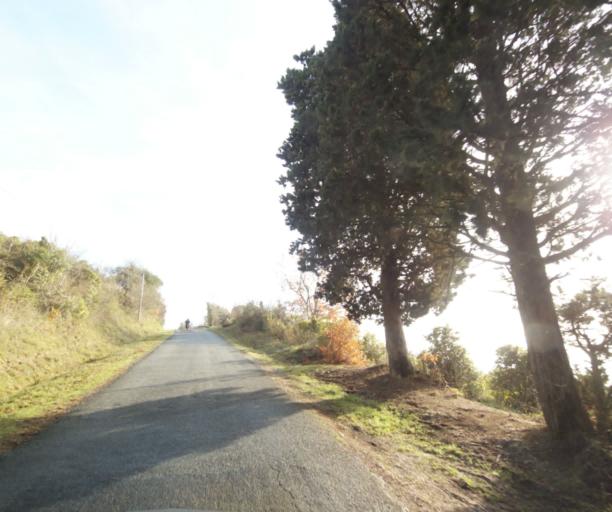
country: FR
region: Midi-Pyrenees
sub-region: Departement de la Haute-Garonne
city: Villemur-sur-Tarn
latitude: 43.8611
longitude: 1.5107
